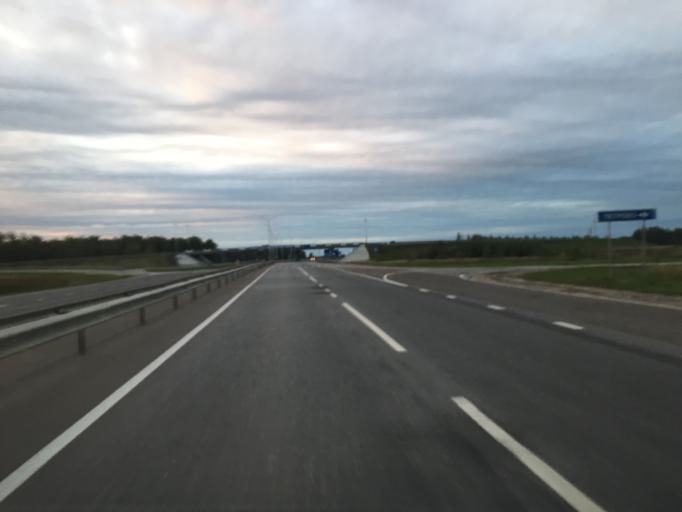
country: RU
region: Kaluga
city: Kaluga
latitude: 54.6226
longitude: 36.2916
